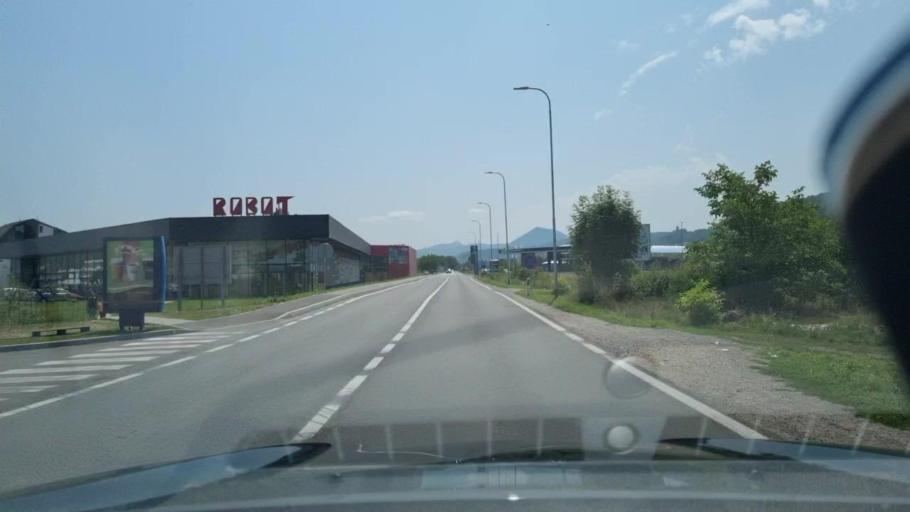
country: BA
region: Federation of Bosnia and Herzegovina
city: Bihac
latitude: 44.8135
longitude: 15.8788
